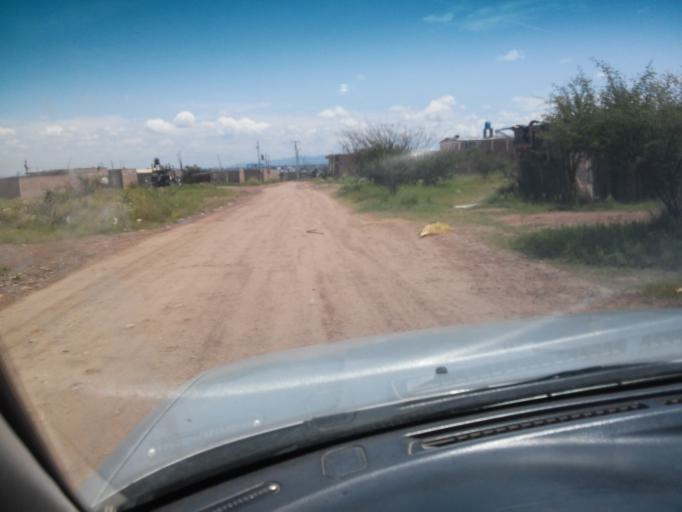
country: MX
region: Durango
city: Victoria de Durango
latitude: 23.9840
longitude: -104.7077
